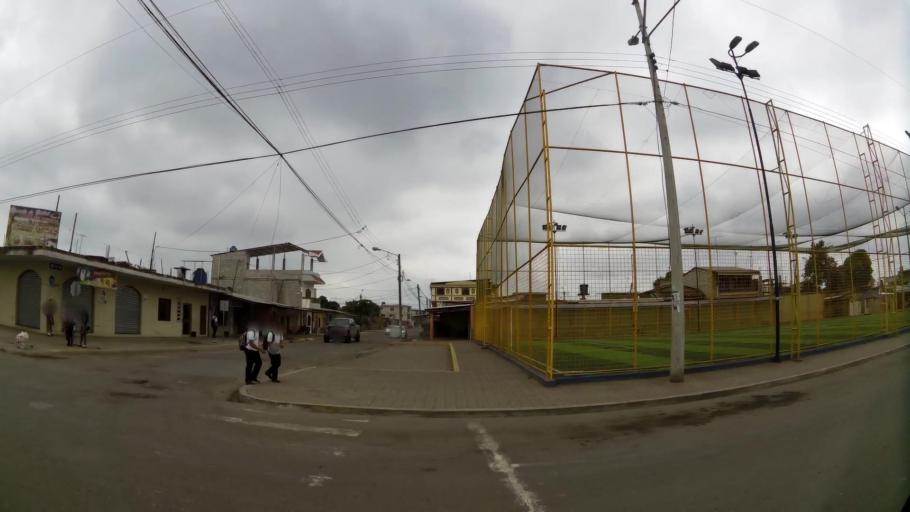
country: EC
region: El Oro
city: Pasaje
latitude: -3.2392
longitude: -79.8296
